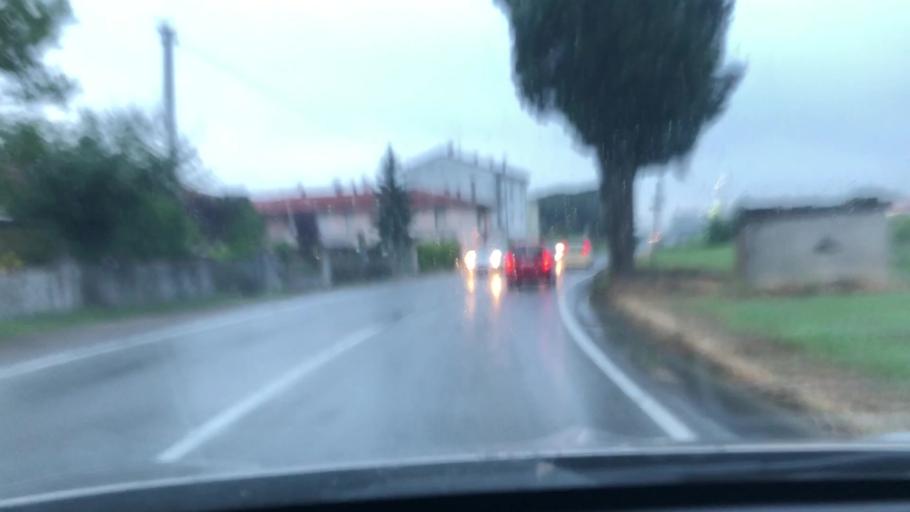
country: IT
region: Tuscany
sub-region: Province of Pisa
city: Val di Cava
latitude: 43.6399
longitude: 10.6507
